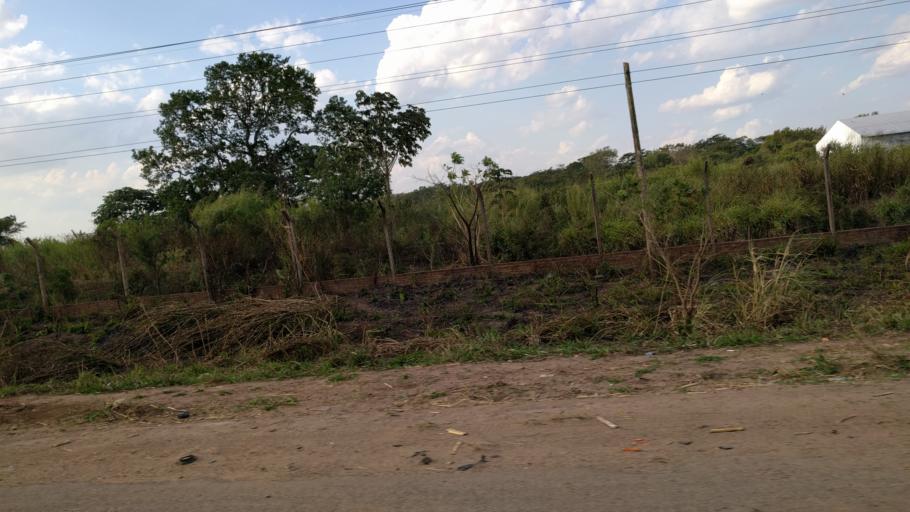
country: BO
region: Santa Cruz
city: Montero
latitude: -17.3720
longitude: -63.2342
